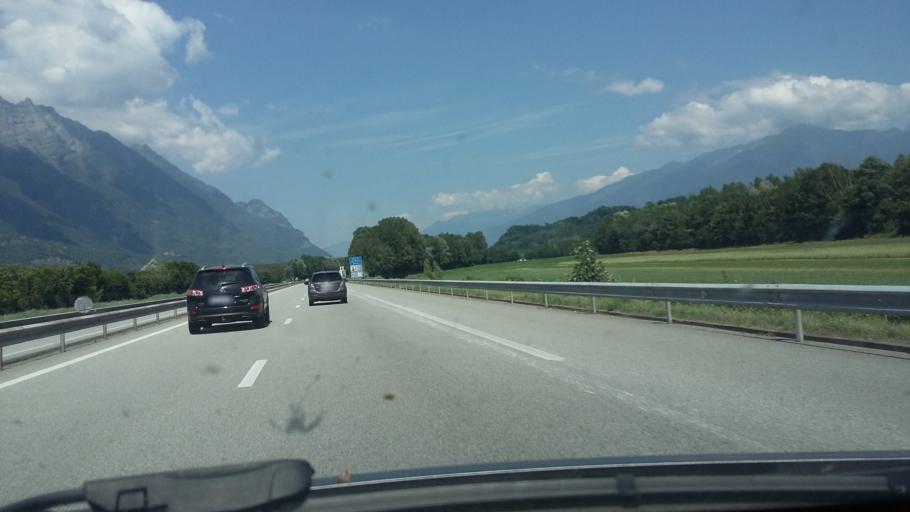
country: FR
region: Rhone-Alpes
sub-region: Departement de la Savoie
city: Coise-Saint-Jean-Pied-Gauthier
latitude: 45.5416
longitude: 6.1404
